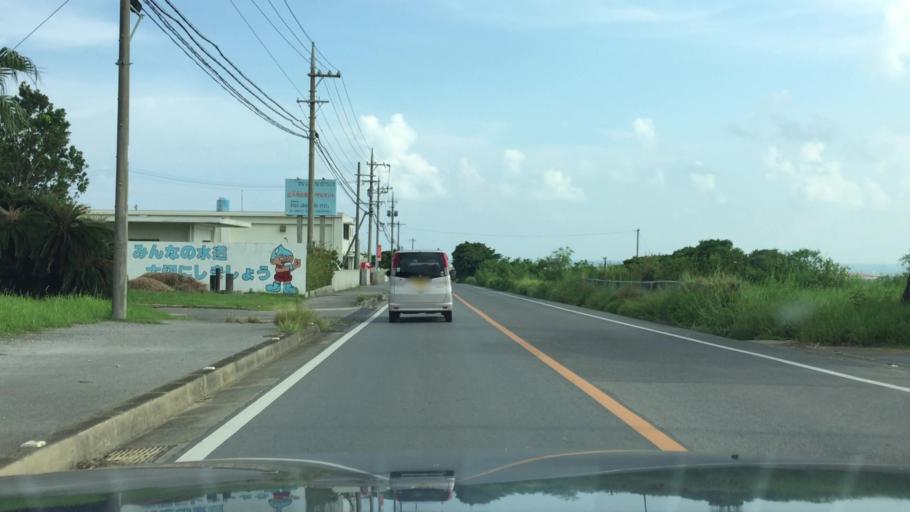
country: JP
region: Okinawa
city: Ishigaki
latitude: 24.3561
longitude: 124.1740
